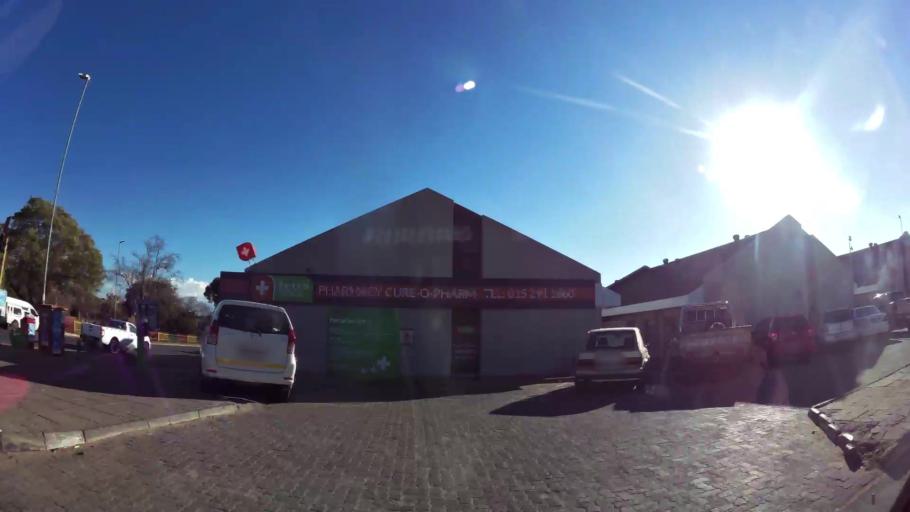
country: ZA
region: Limpopo
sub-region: Capricorn District Municipality
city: Polokwane
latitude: -23.9092
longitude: 29.4634
